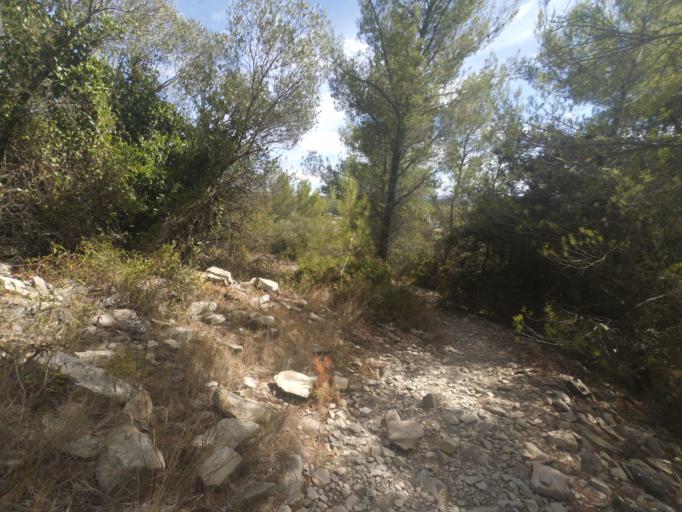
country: FR
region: Languedoc-Roussillon
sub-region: Departement du Gard
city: Nages-et-Solorgues
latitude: 43.7933
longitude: 4.2272
